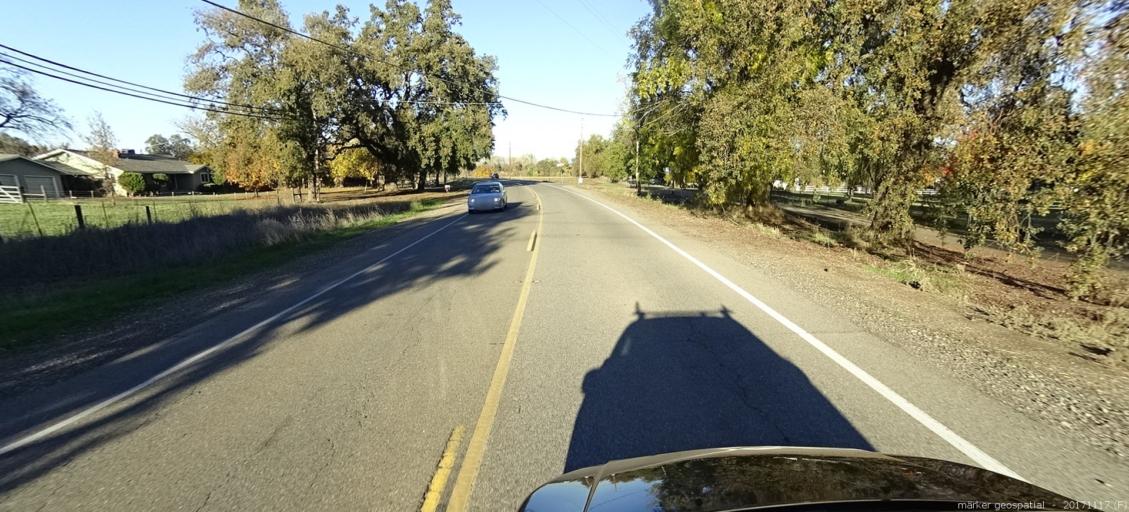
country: US
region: California
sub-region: Shasta County
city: Anderson
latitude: 40.4573
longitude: -122.2460
